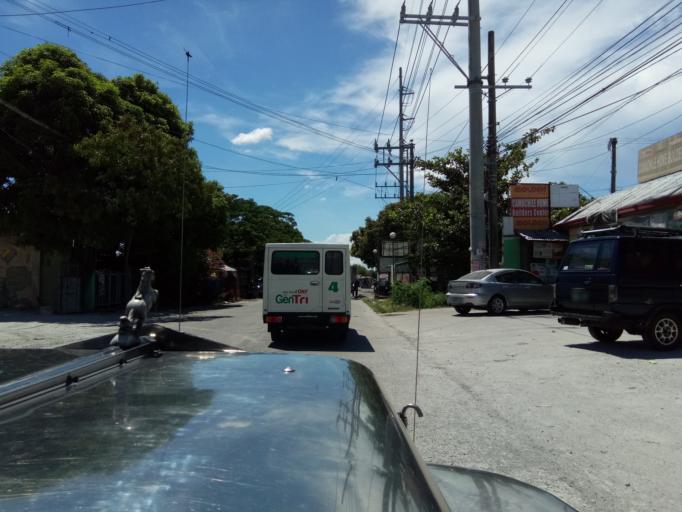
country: PH
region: Calabarzon
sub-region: Province of Cavite
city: General Trias
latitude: 14.3692
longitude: 120.8903
